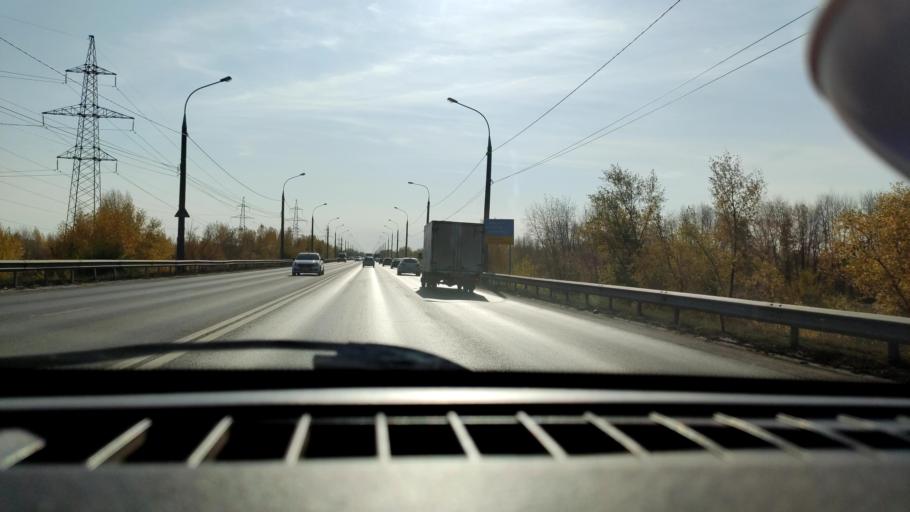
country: RU
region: Samara
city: Samara
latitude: 53.1640
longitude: 50.1962
